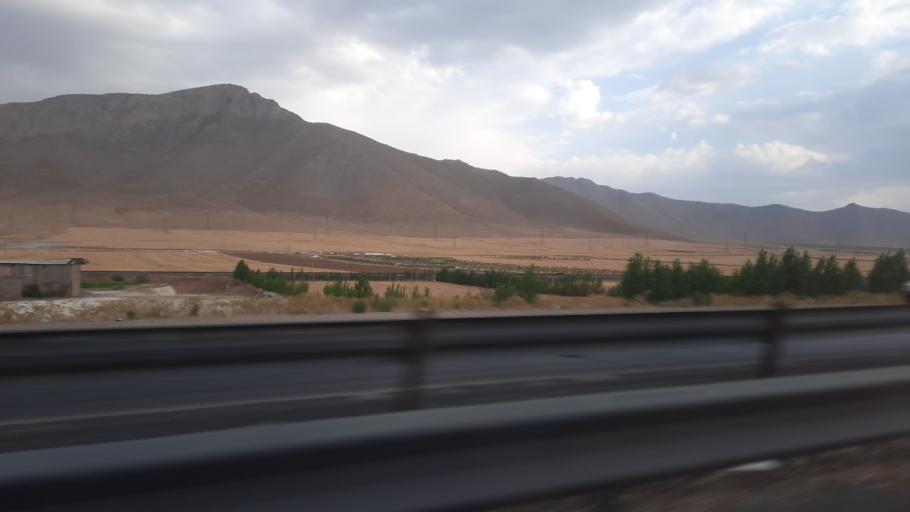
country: IR
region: Markazi
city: Shazand
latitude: 34.0142
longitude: 49.5461
